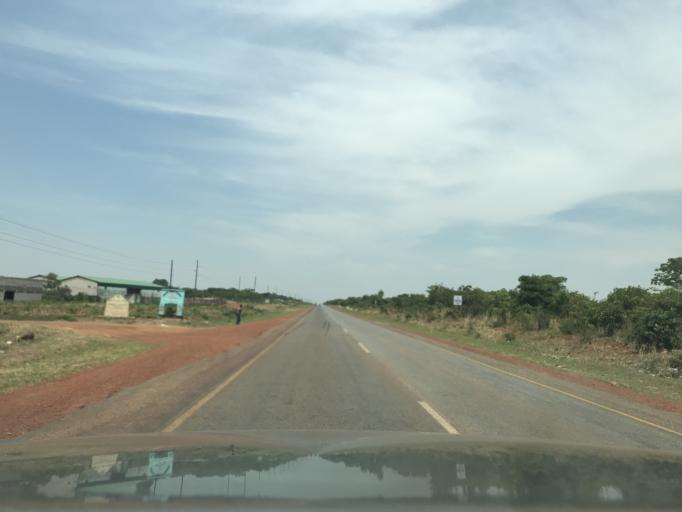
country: ZM
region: Northern
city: Kasama
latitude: -10.2205
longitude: 31.1245
